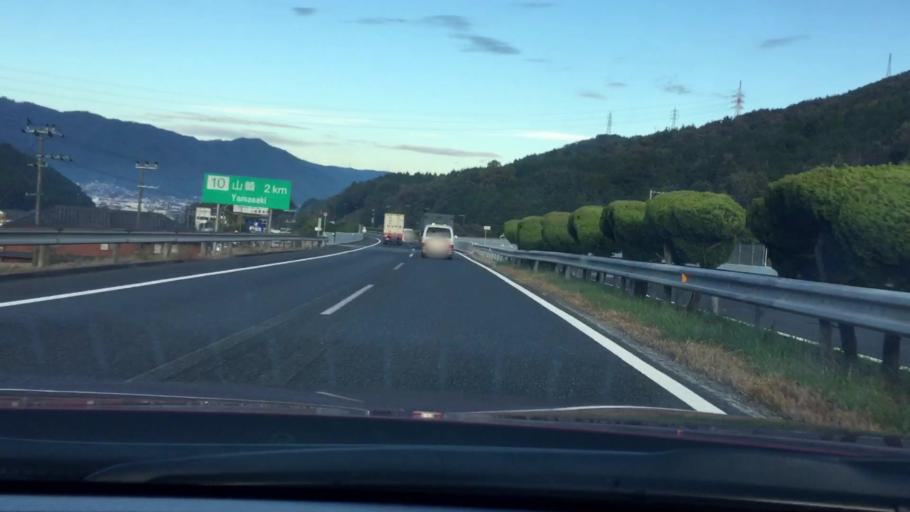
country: JP
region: Hyogo
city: Yamazakicho-nakabirose
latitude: 34.9935
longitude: 134.5723
